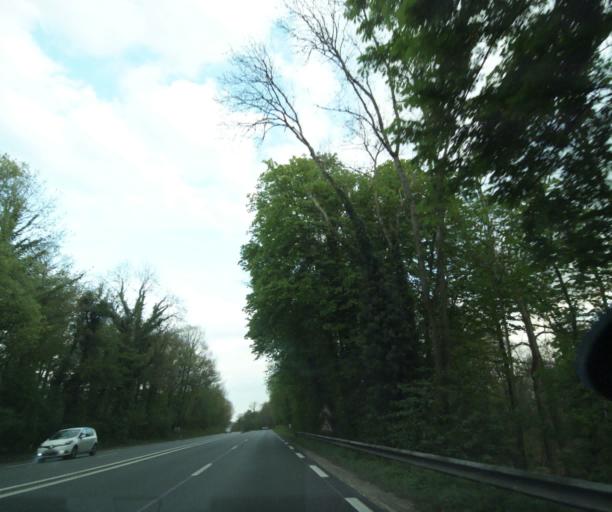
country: FR
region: Ile-de-France
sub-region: Departement de Seine-et-Marne
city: Fontainebleau
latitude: 48.4163
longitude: 2.6751
